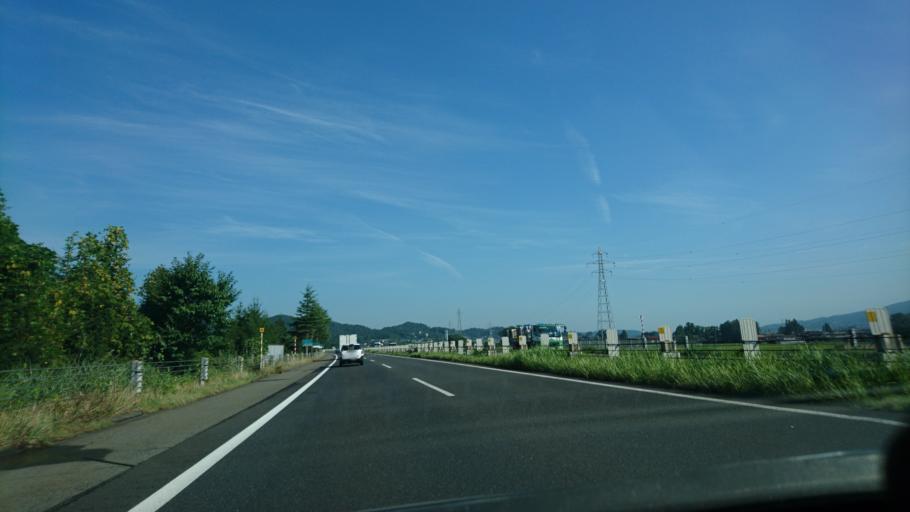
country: JP
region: Iwate
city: Ichinoseki
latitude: 38.9737
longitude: 141.1119
